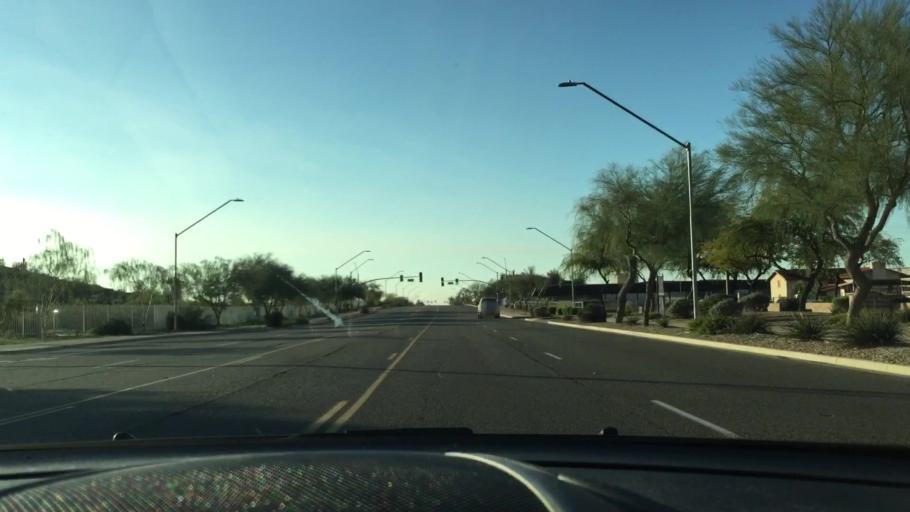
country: US
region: Arizona
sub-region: Maricopa County
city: Sun City
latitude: 33.6943
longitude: -112.2031
